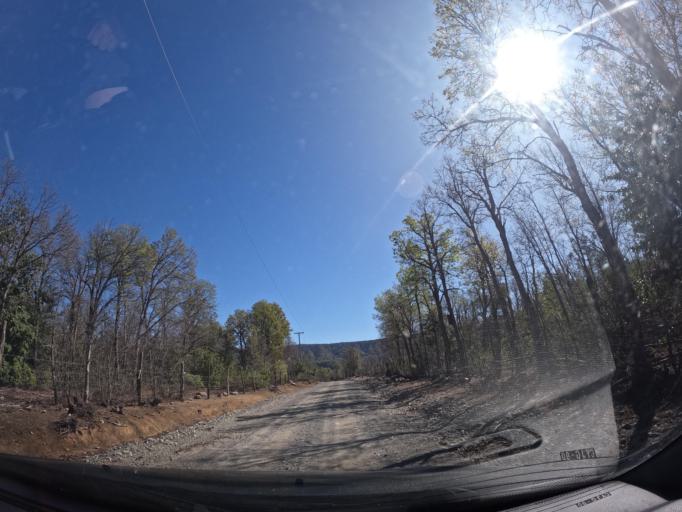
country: CL
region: Maule
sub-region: Provincia de Linares
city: Longavi
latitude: -36.2384
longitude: -71.3554
